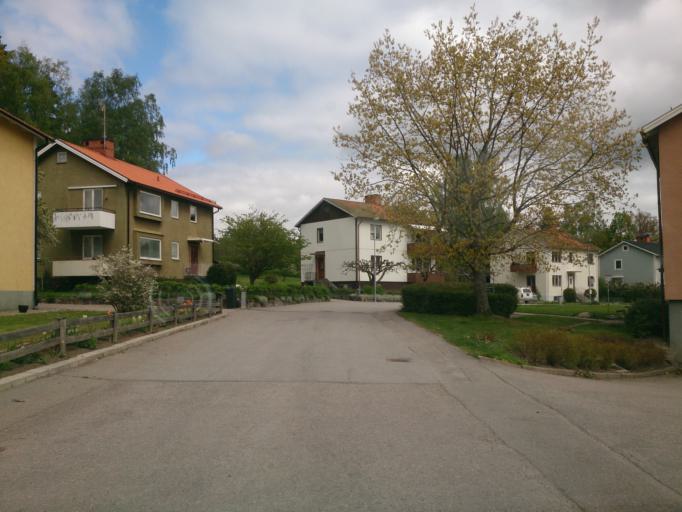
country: SE
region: OEstergoetland
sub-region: Atvidabergs Kommun
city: Atvidaberg
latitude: 58.2061
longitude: 16.0035
